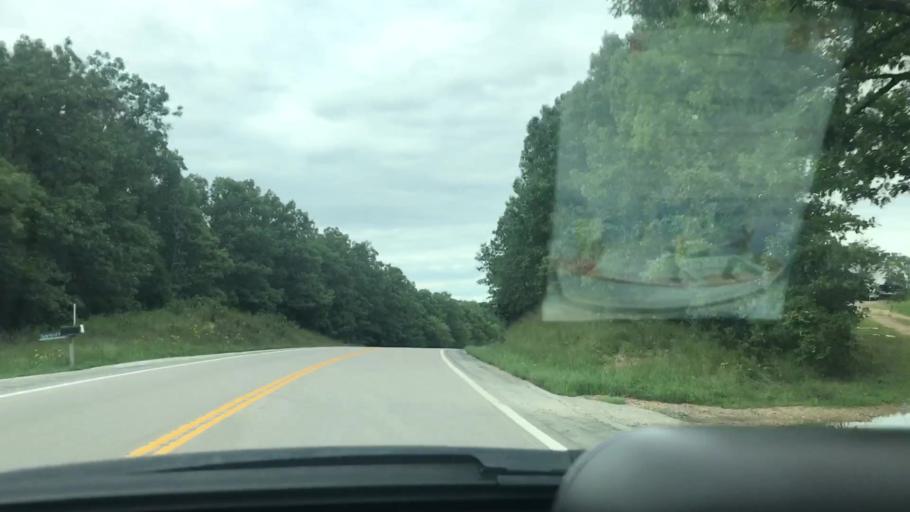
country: US
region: Missouri
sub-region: Benton County
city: Warsaw
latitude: 38.1653
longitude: -93.3075
